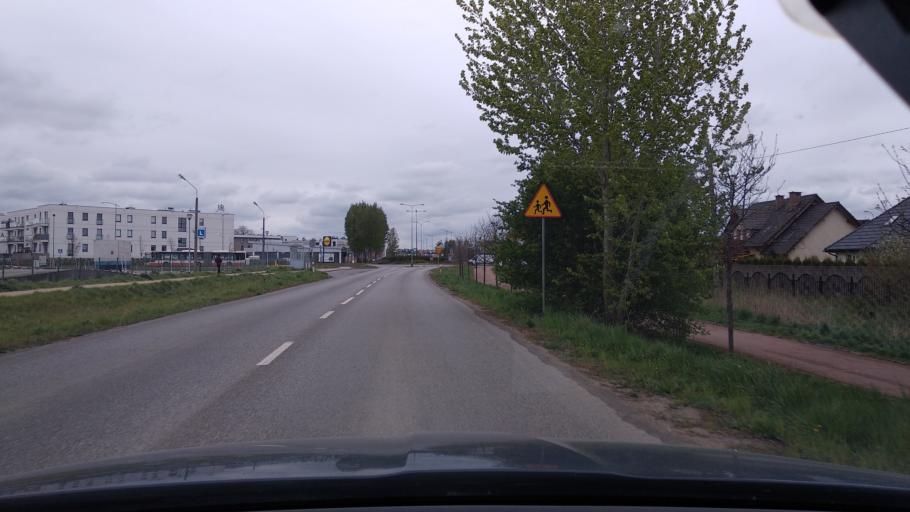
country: PL
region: Pomeranian Voivodeship
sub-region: Powiat gdanski
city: Pruszcz Gdanski
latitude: 54.2656
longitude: 18.6681
